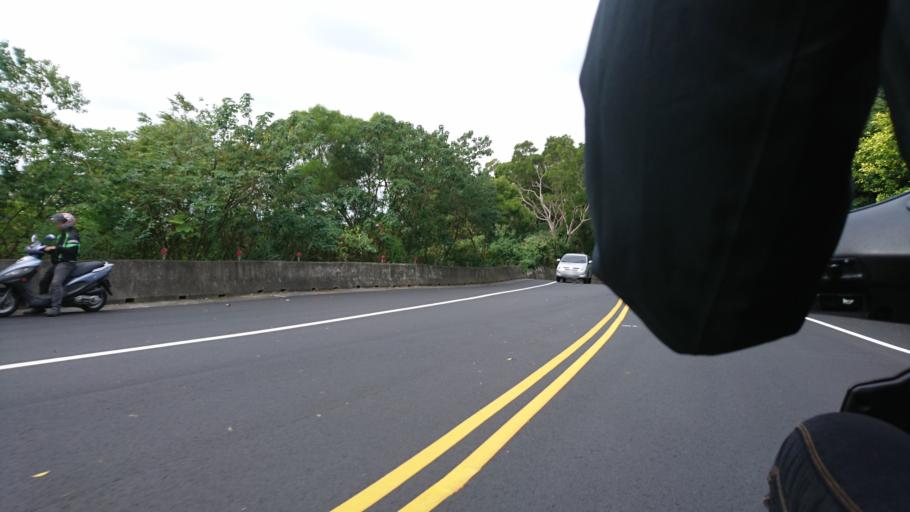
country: TW
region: Taiwan
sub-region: Hsinchu
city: Hsinchu
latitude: 24.7880
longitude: 120.9569
